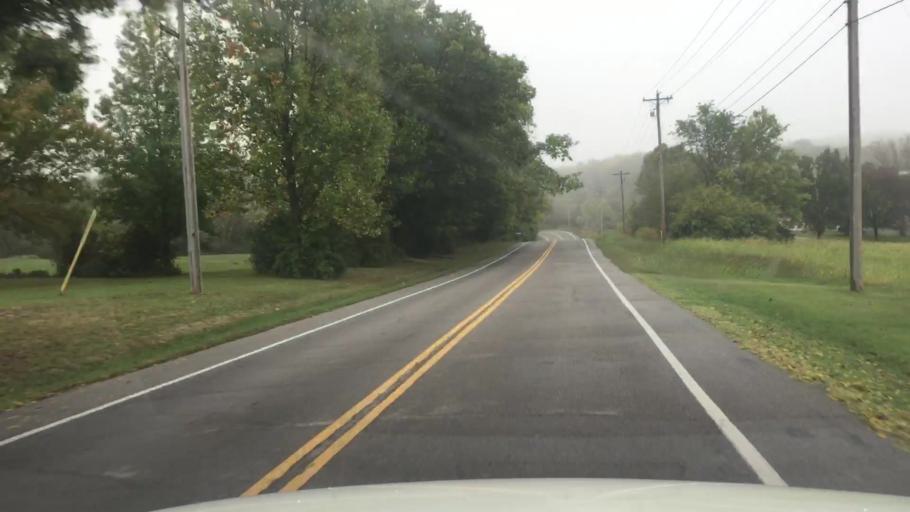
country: US
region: Missouri
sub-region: Boone County
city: Columbia
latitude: 38.8724
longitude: -92.4113
